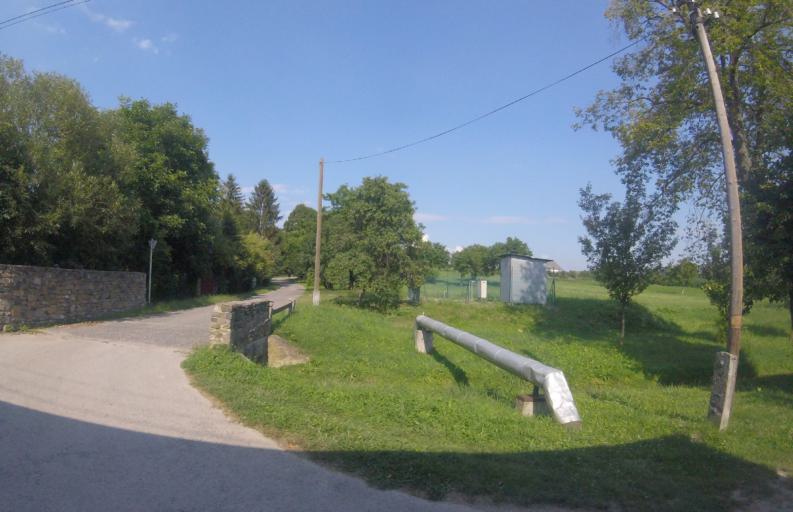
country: HU
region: Zala
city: Cserszegtomaj
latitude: 46.8855
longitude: 17.1944
